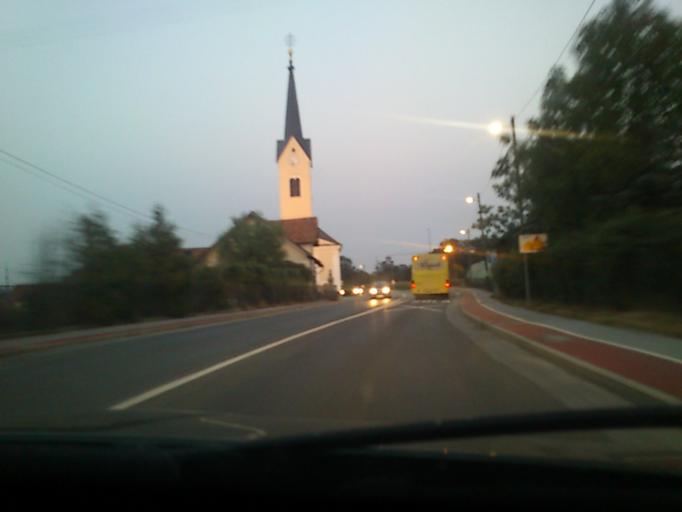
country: SI
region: Starse
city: Starse
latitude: 46.4666
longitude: 15.7664
